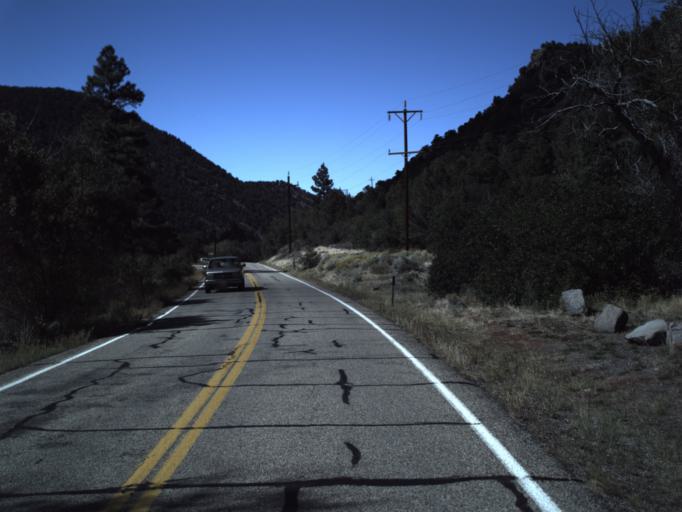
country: US
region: Utah
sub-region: Beaver County
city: Beaver
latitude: 38.2546
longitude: -112.5400
